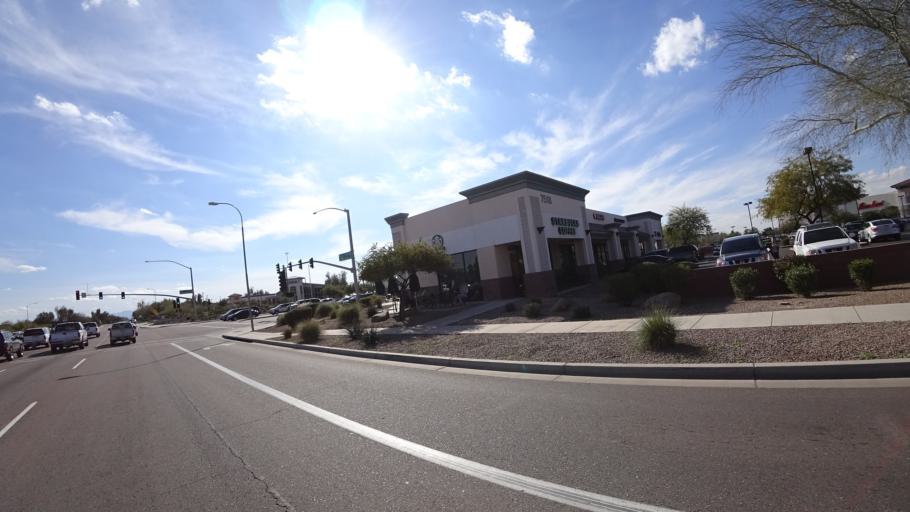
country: US
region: Arizona
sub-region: Maricopa County
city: Peoria
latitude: 33.6108
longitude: -112.2202
